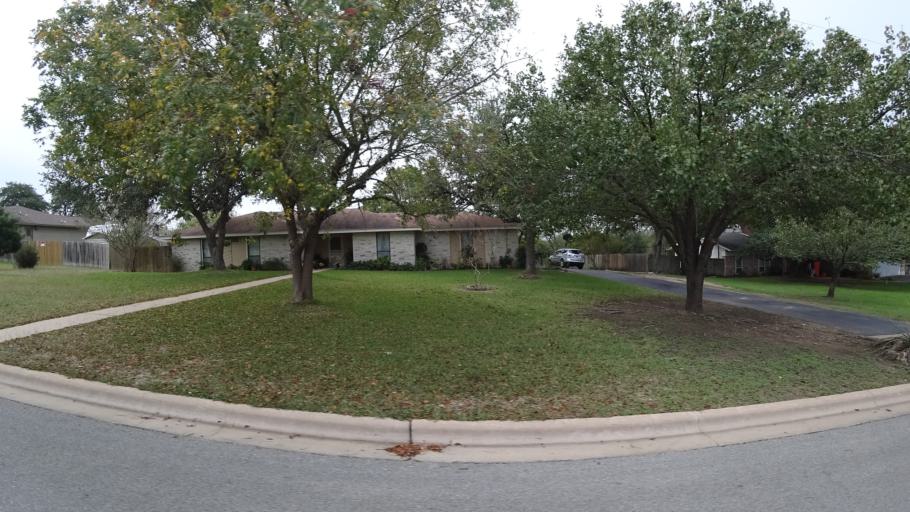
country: US
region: Texas
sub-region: Travis County
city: Shady Hollow
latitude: 30.2192
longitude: -97.8983
